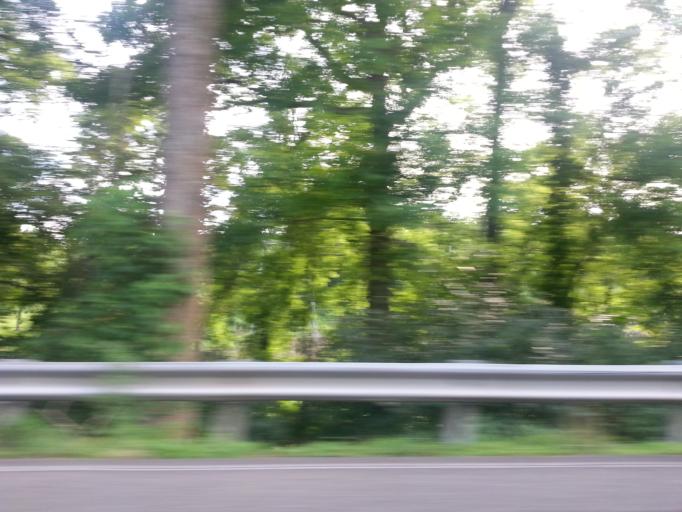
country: US
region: Tennessee
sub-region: Knox County
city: Farragut
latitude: 35.9085
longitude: -84.0762
